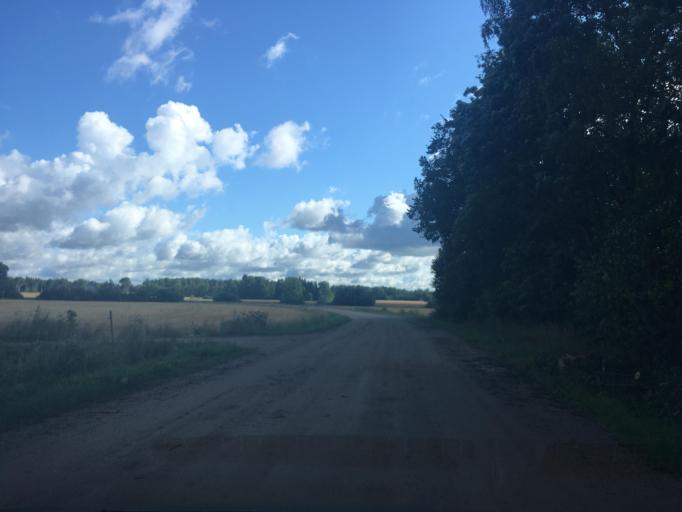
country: EE
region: Jogevamaa
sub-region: Poltsamaa linn
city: Poltsamaa
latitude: 58.4763
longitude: 25.9627
